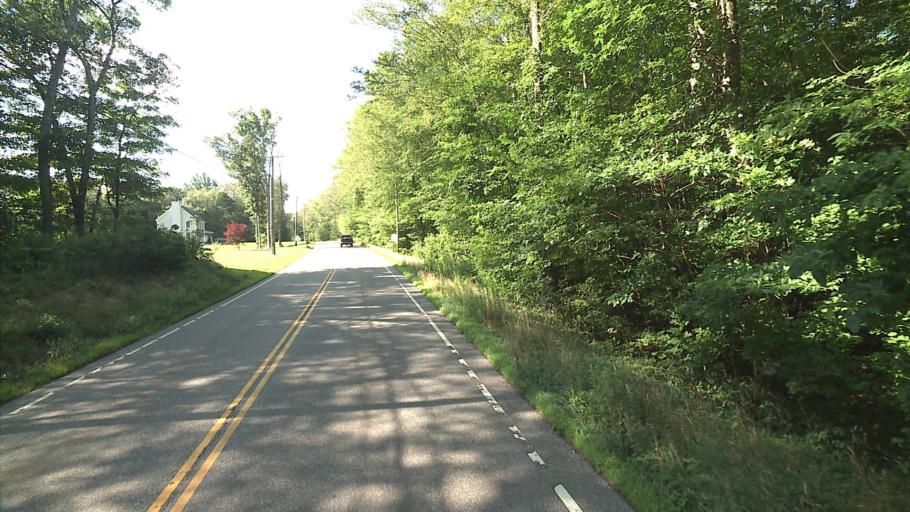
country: US
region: Connecticut
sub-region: New London County
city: Montville Center
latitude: 41.5264
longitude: -72.2067
